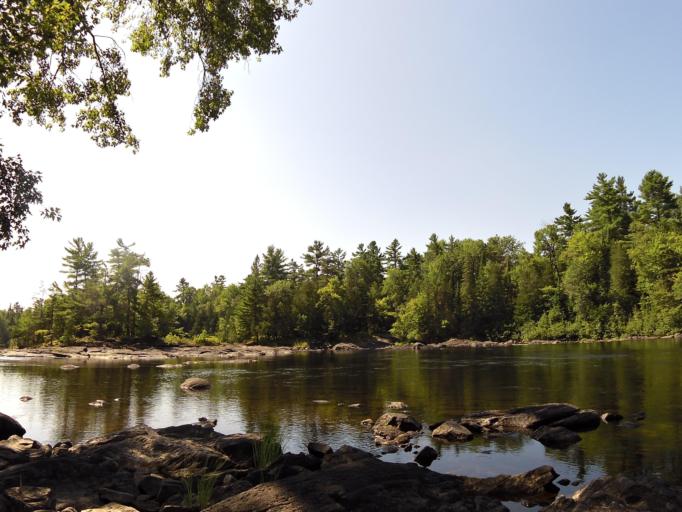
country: CA
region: Ontario
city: Renfrew
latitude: 45.2538
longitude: -77.1942
